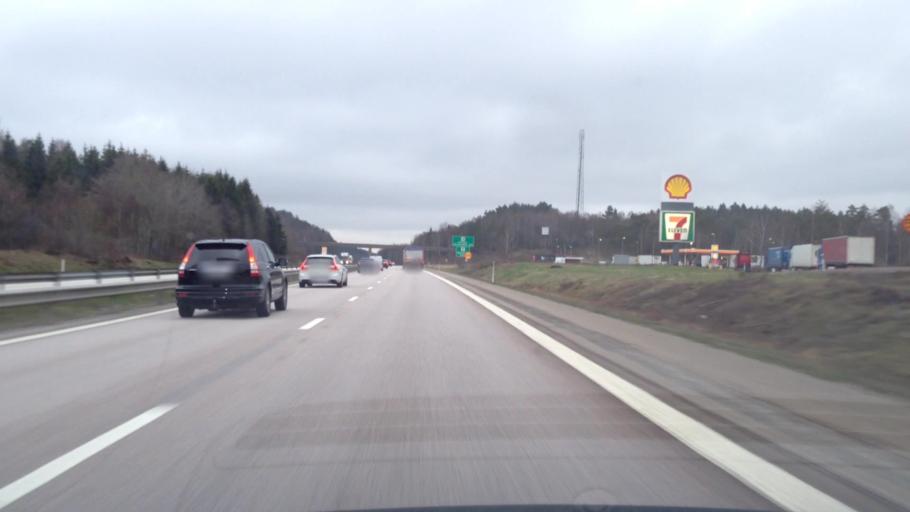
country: SE
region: Vaestra Goetaland
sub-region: Molndal
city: Lindome
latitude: 57.5488
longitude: 12.0532
